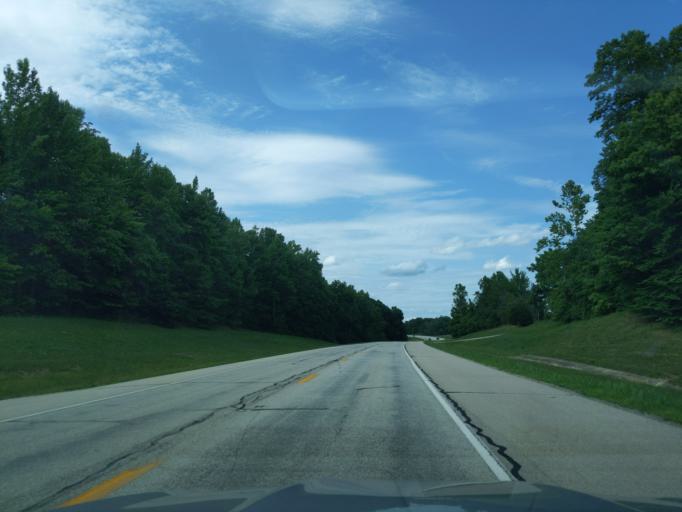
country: US
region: Indiana
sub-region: Ripley County
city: Batesville
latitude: 39.2177
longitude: -85.2093
